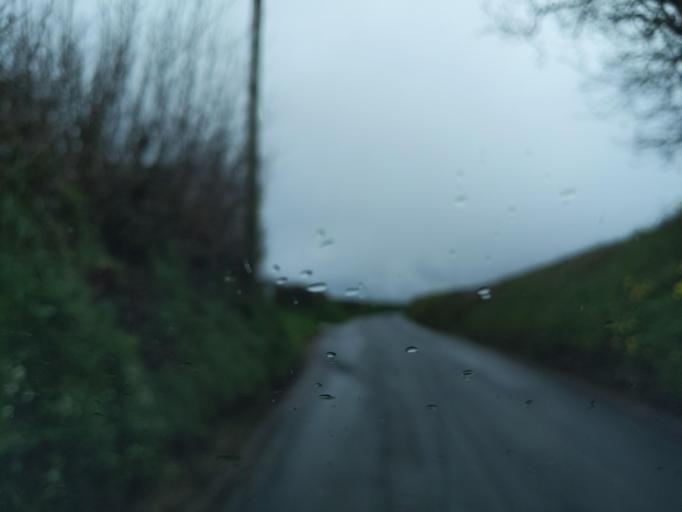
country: GB
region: England
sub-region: Cornwall
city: North Hill
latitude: 50.5840
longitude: -4.4339
